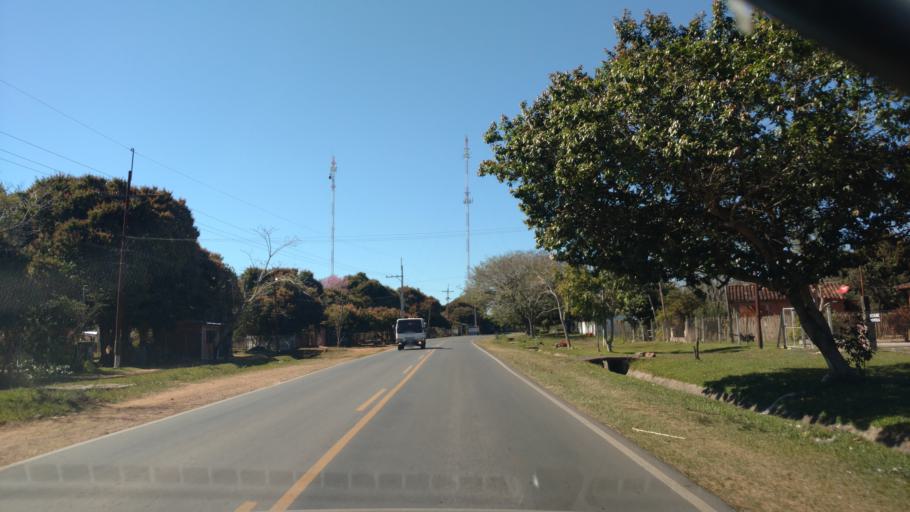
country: PY
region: Paraguari
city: Pirayu
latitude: -25.4744
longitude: -57.2504
